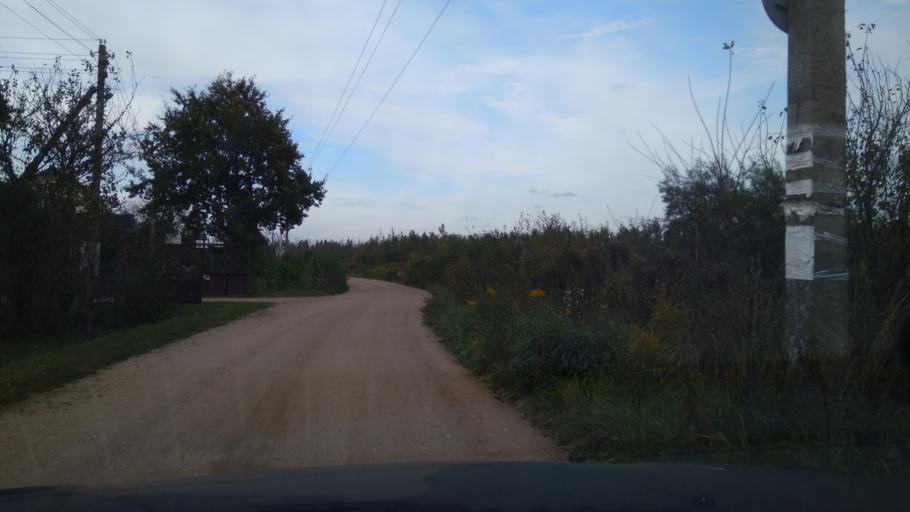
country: BY
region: Minsk
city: Rudzyensk
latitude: 53.6082
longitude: 27.8483
